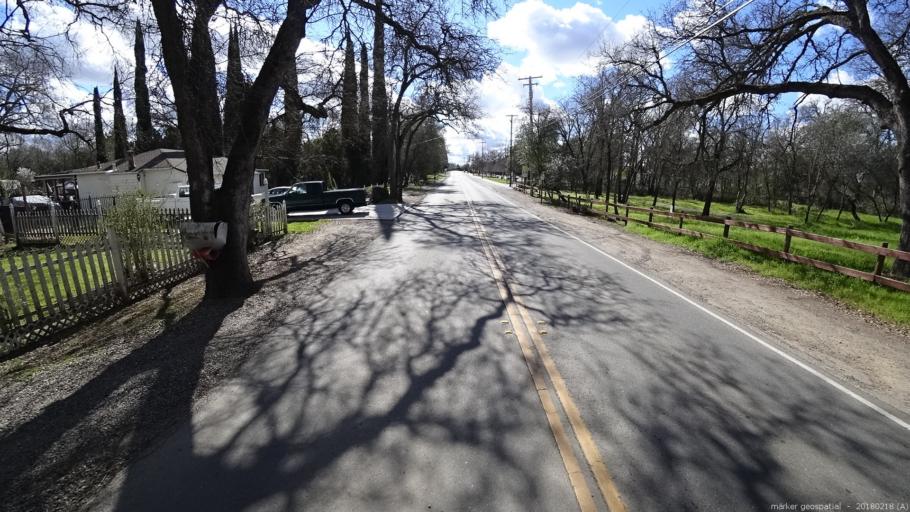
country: US
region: California
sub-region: Sacramento County
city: Orangevale
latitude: 38.6978
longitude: -121.2156
